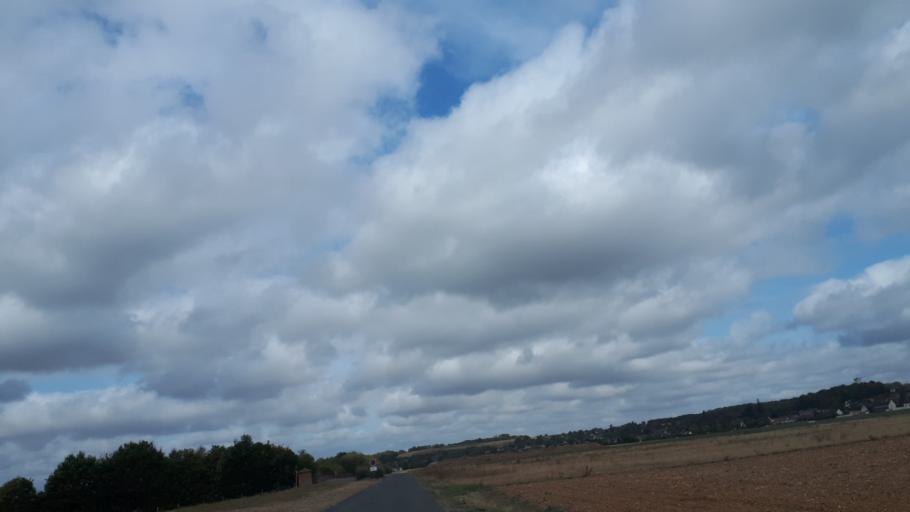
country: FR
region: Centre
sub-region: Departement du Loir-et-Cher
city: Villiers-sur-Loir
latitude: 47.7944
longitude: 0.9964
